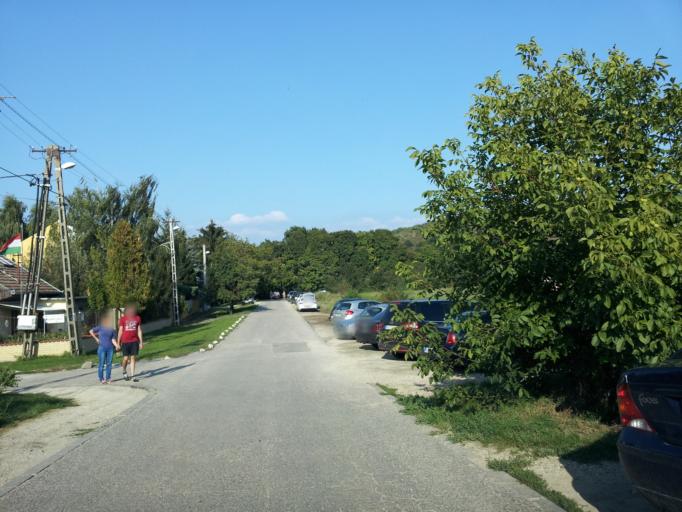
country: HU
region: Pest
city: Solymar
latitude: 47.5546
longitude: 18.9693
